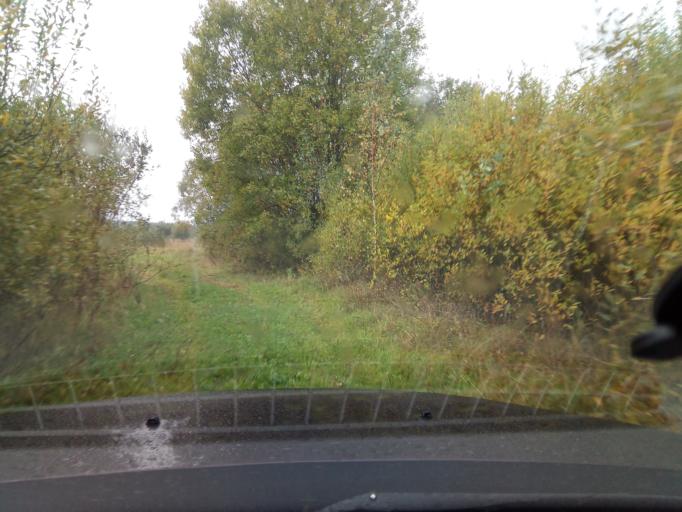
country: LT
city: Skaidiskes
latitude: 54.5978
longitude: 25.5851
